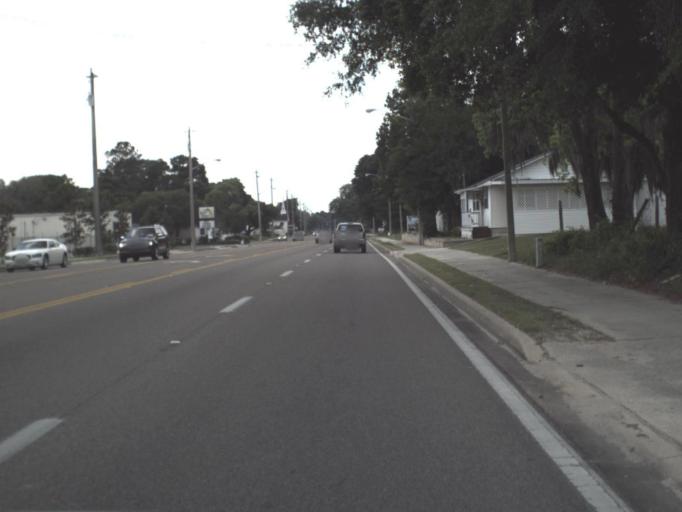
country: US
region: Florida
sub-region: Columbia County
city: Lake City
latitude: 30.1834
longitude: -82.6284
